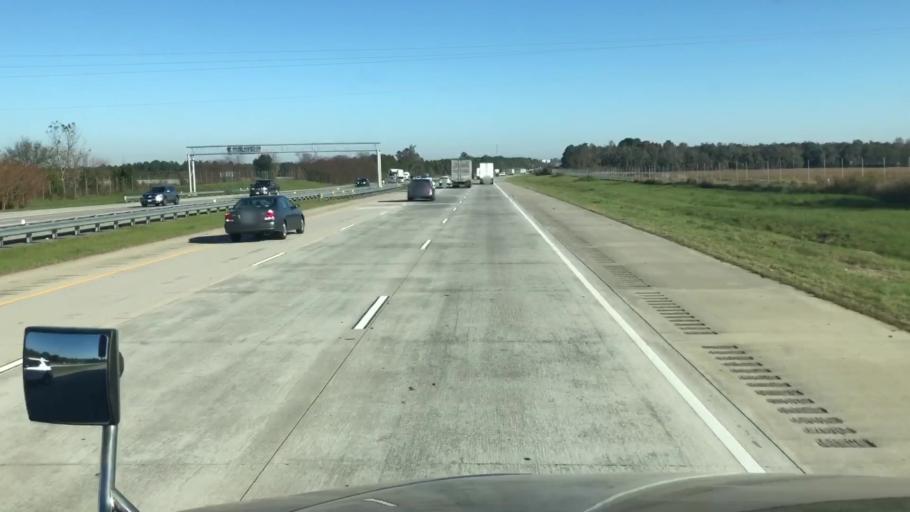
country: US
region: Georgia
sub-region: Dooly County
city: Unadilla
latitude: 32.2119
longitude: -83.7455
